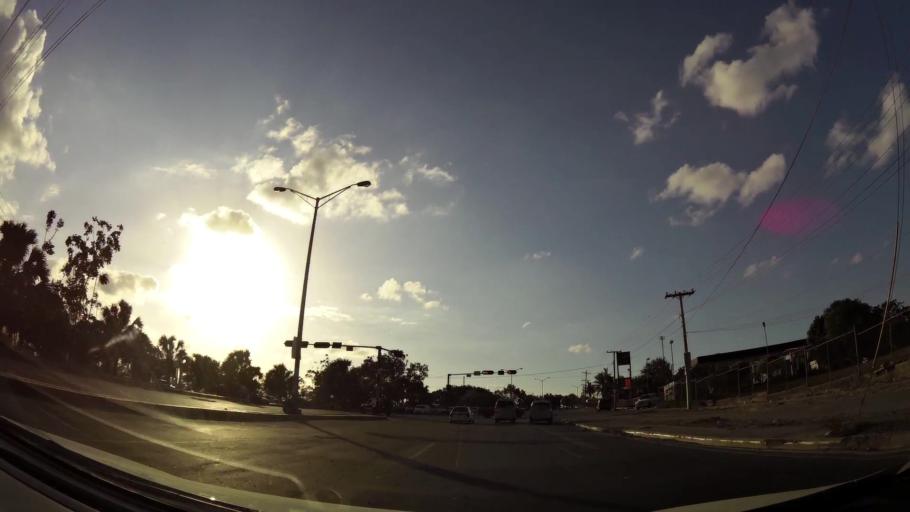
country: DO
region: Nacional
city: La Agustina
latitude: 18.5469
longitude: -69.9206
